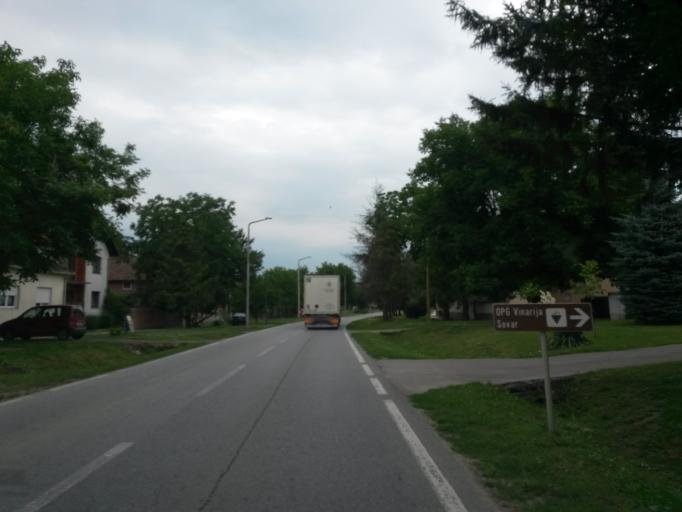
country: HR
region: Vukovarsko-Srijemska
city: Negoslavci
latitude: 45.2993
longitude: 19.0930
